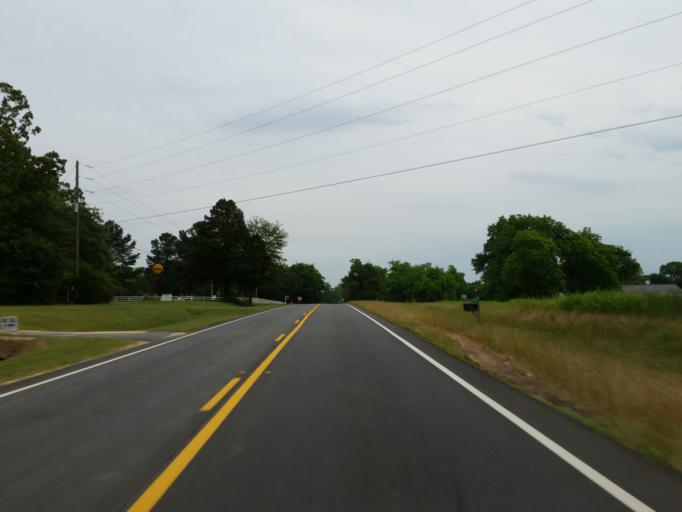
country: US
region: Georgia
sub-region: Dooly County
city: Unadilla
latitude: 32.3456
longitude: -83.7892
